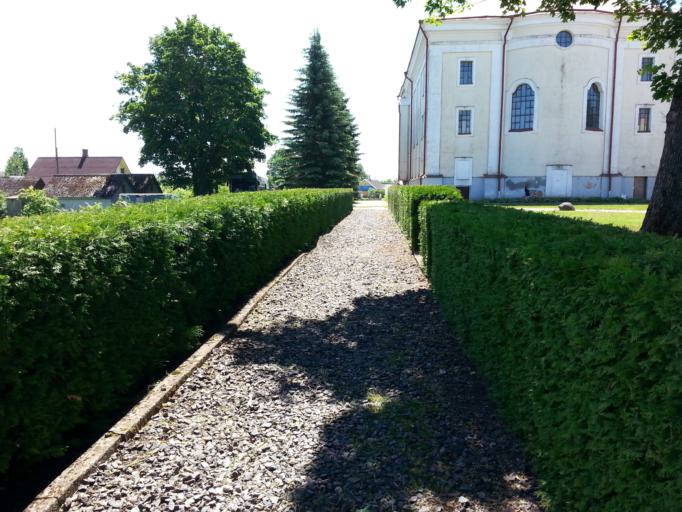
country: BY
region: Vitebsk
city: Mosar
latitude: 55.2113
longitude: 27.5593
